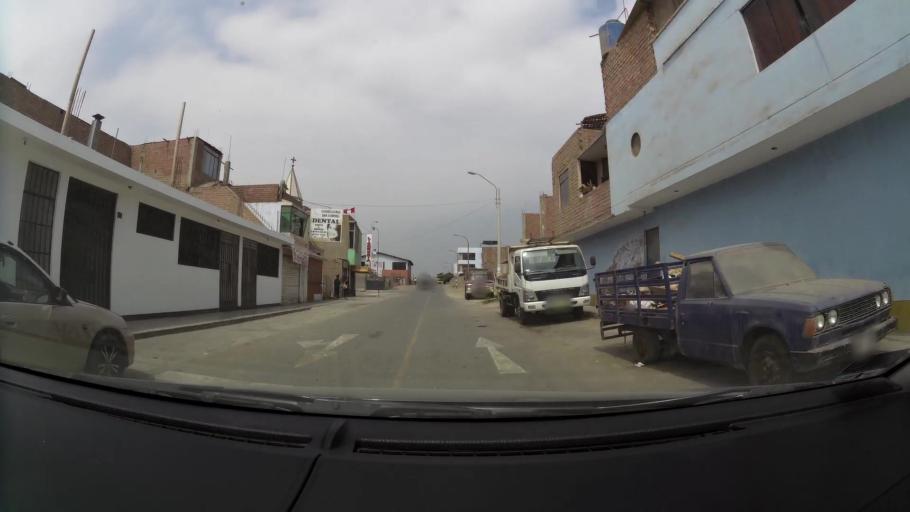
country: PE
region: Lima
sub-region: Lima
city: Santa Rosa
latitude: -11.7869
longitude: -77.1562
